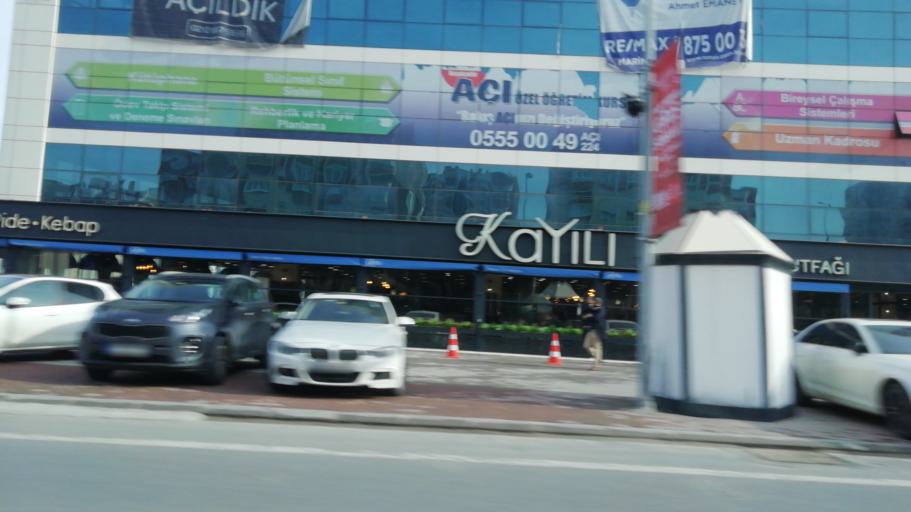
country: TR
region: Istanbul
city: Basaksehir
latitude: 41.1042
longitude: 28.7941
